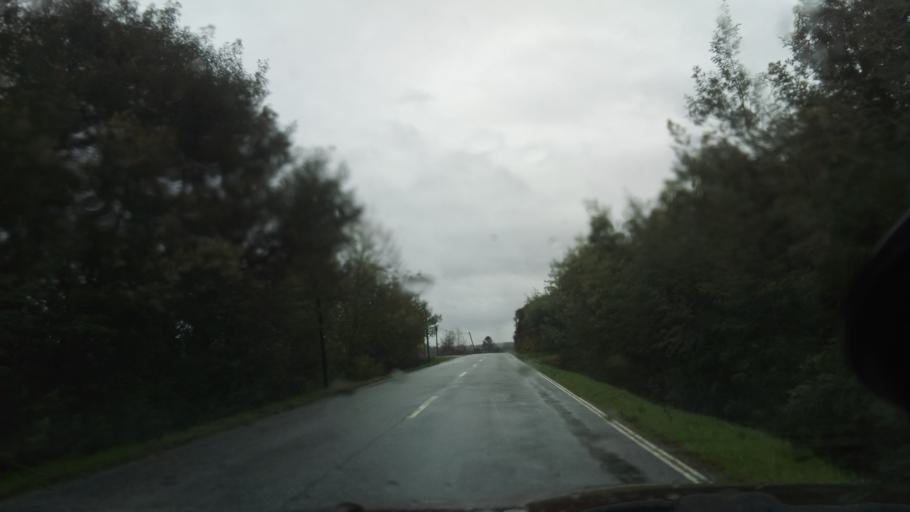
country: PT
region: Guarda
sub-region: Fornos de Algodres
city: Fornos de Algodres
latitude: 40.6181
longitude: -7.4969
